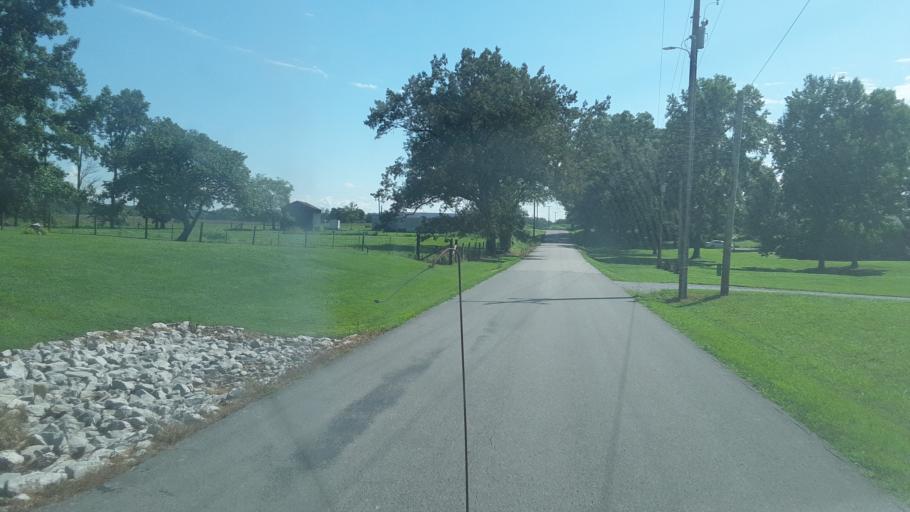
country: US
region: Kentucky
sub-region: Todd County
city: Elkton
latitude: 36.7967
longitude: -87.1974
